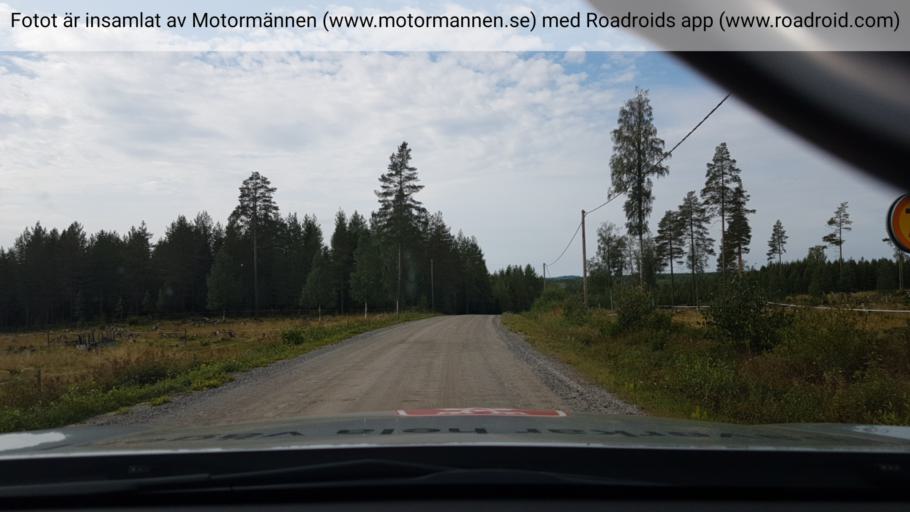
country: SE
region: Vaesterbotten
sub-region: Vannas Kommun
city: Vaennaes
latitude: 63.8725
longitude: 19.5703
